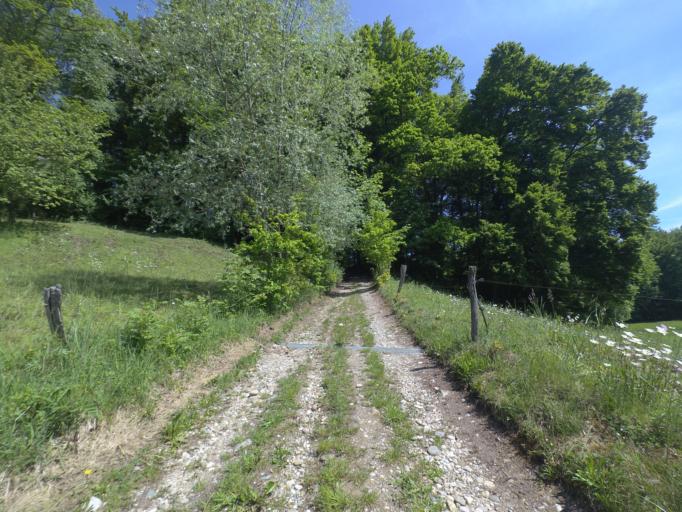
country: DE
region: Bavaria
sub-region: Upper Bavaria
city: Petting
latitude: 47.8986
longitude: 12.8086
